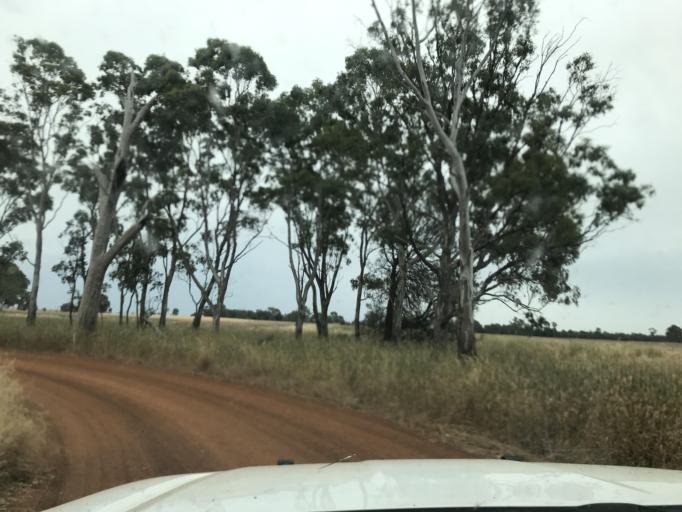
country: AU
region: Victoria
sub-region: Horsham
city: Horsham
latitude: -37.0650
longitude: 141.6757
